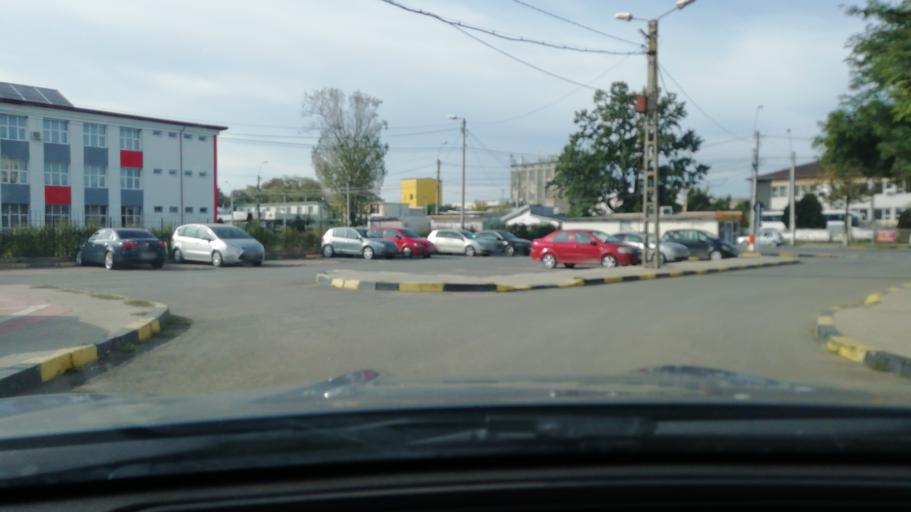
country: RO
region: Galati
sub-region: Municipiul Tecuci
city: Tecuci
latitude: 45.8301
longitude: 27.4378
